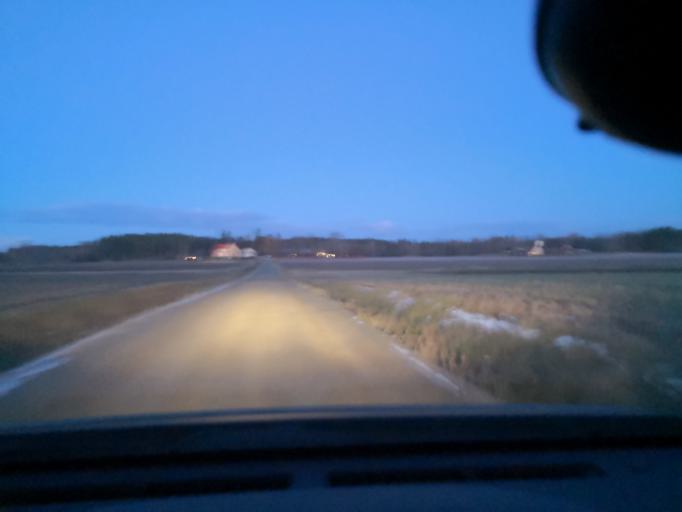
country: SE
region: Vaestmanland
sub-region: Sala Kommun
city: Sala
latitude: 59.8737
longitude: 16.6916
